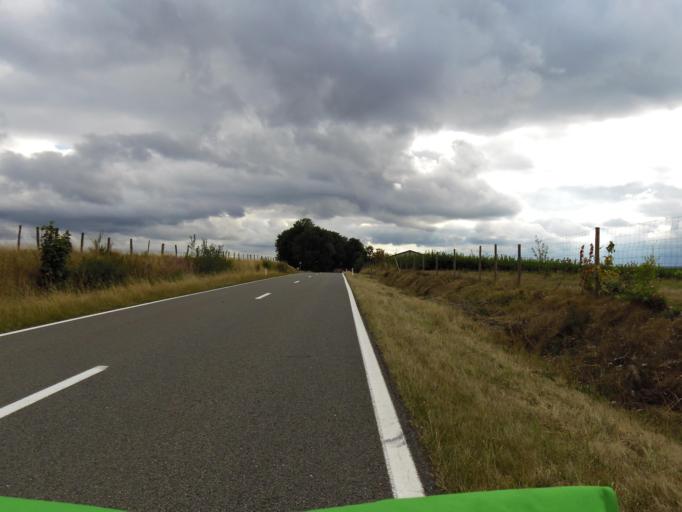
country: BE
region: Wallonia
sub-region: Province de Namur
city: Bievre
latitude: 49.9147
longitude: 4.9960
